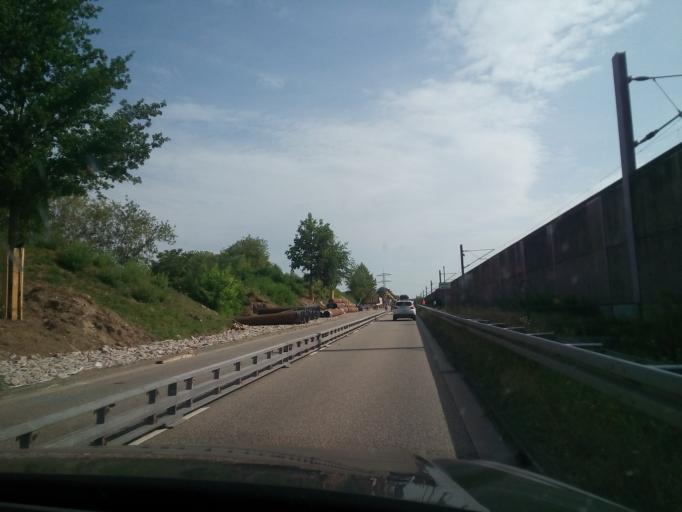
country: DE
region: Baden-Wuerttemberg
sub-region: Karlsruhe Region
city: Sinzheim
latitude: 48.7674
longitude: 8.1658
